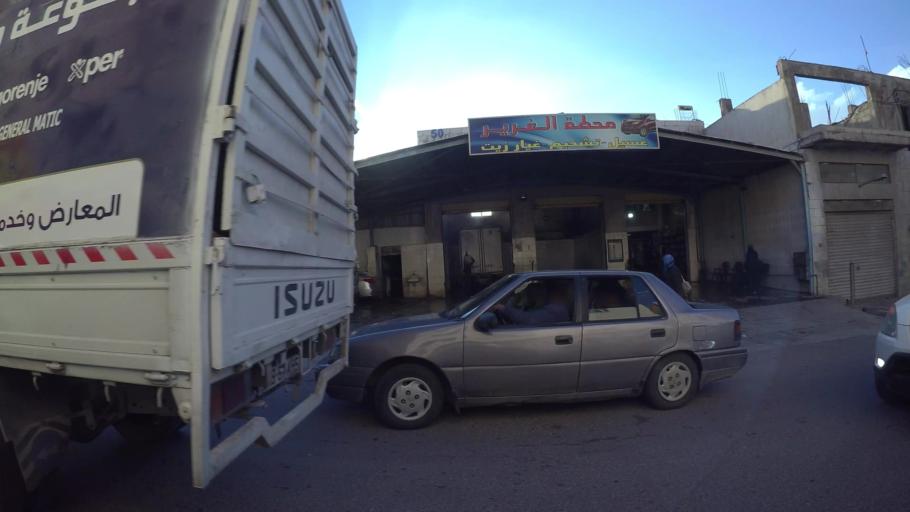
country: JO
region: Amman
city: Al Bunayyat ash Shamaliyah
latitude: 31.9070
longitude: 35.9121
